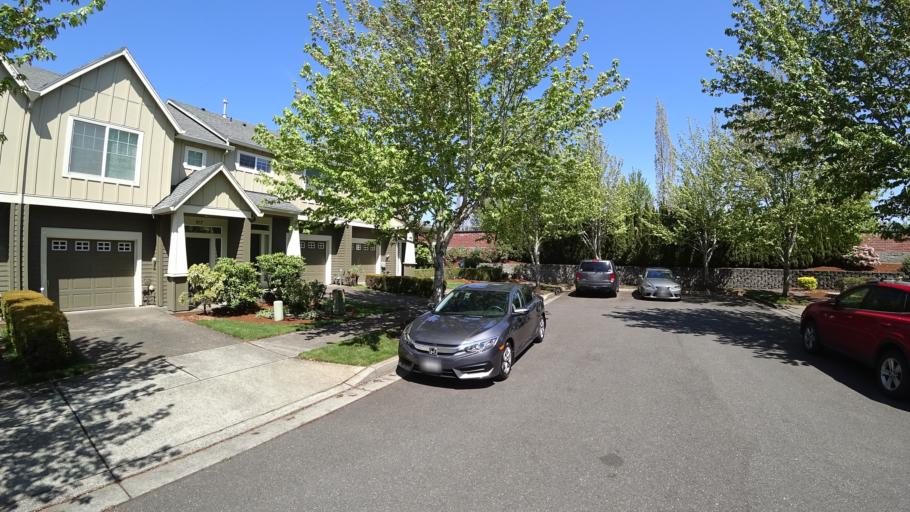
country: US
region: Oregon
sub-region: Washington County
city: Hillsboro
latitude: 45.5111
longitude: -122.9730
